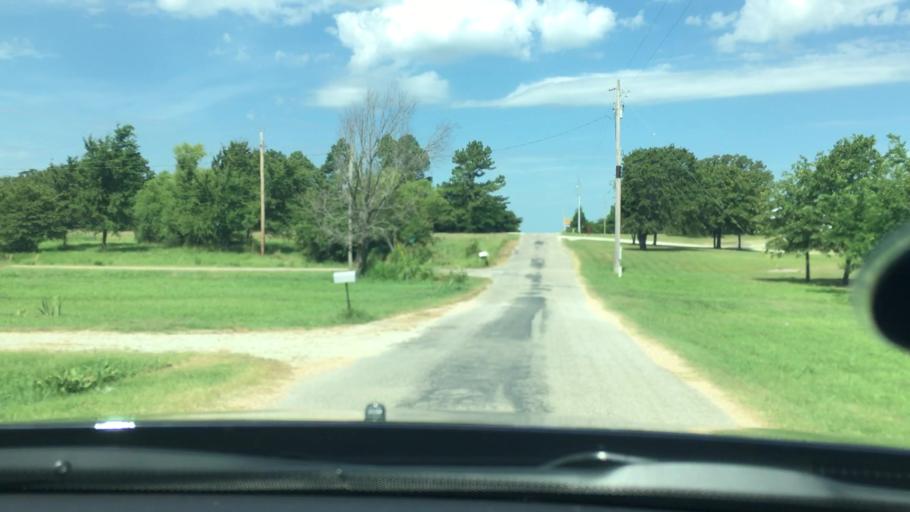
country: US
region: Oklahoma
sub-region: Pontotoc County
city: Ada
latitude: 34.7636
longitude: -96.5671
